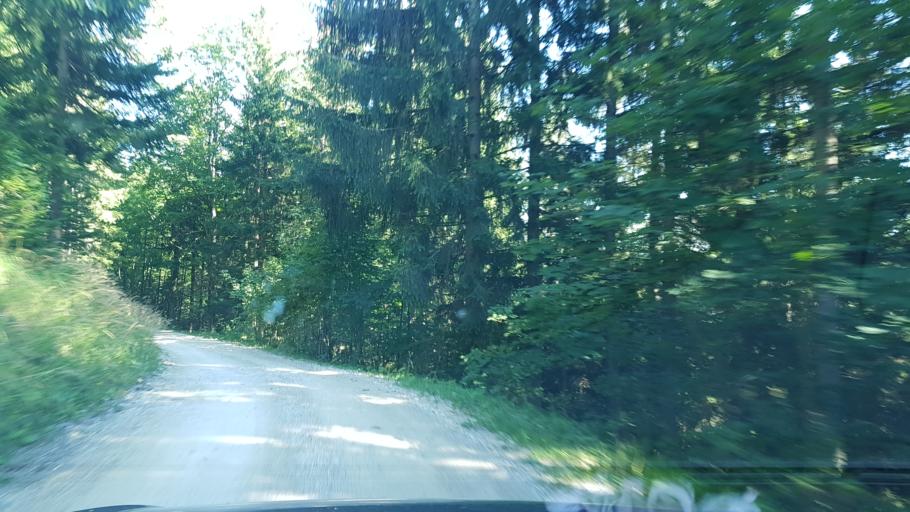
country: SI
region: Ravne na Koroskem
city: Kotlje
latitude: 46.4802
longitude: 14.9480
